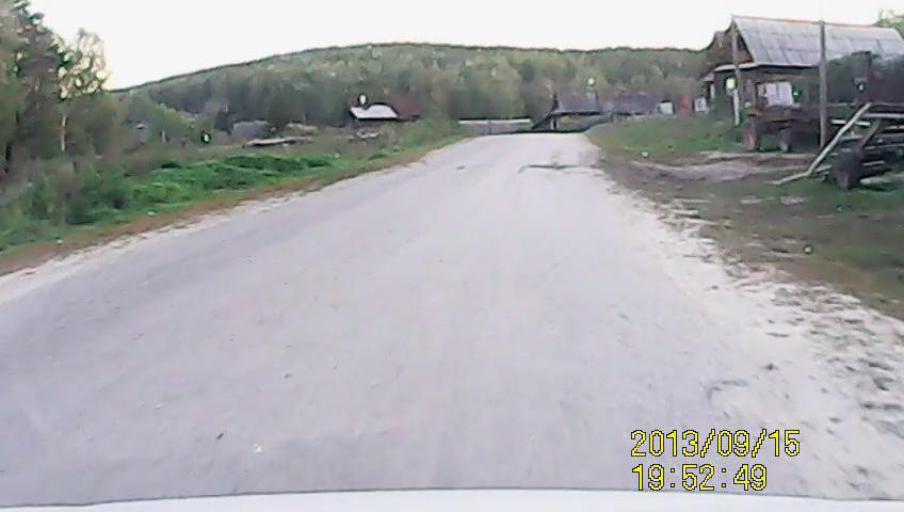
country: RU
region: Chelyabinsk
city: Kyshtym
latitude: 55.7666
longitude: 60.4866
